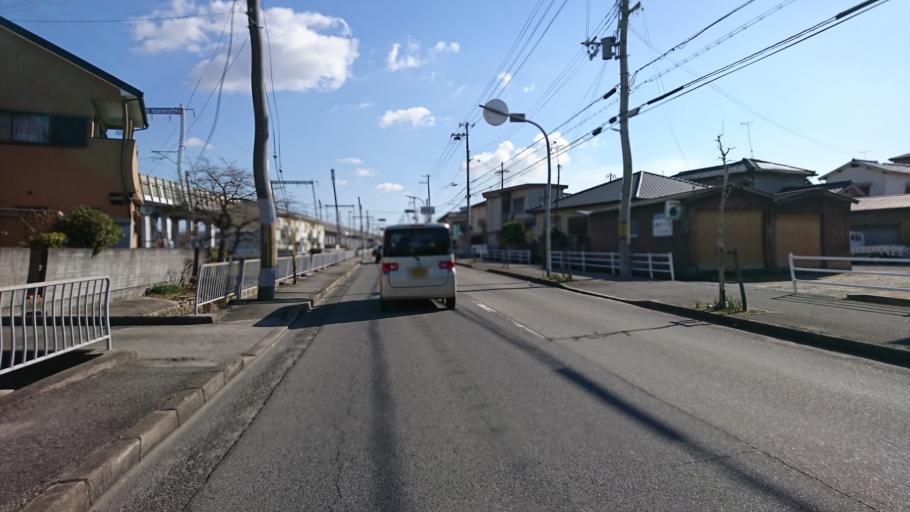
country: JP
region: Hyogo
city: Kakogawacho-honmachi
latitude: 34.7733
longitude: 134.7906
